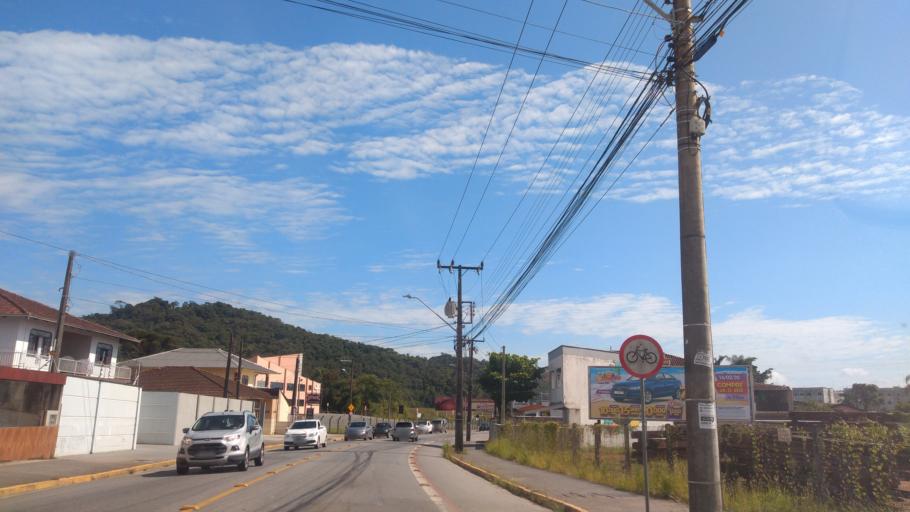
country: BR
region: Santa Catarina
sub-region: Joinville
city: Joinville
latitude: -26.2482
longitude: -48.8215
